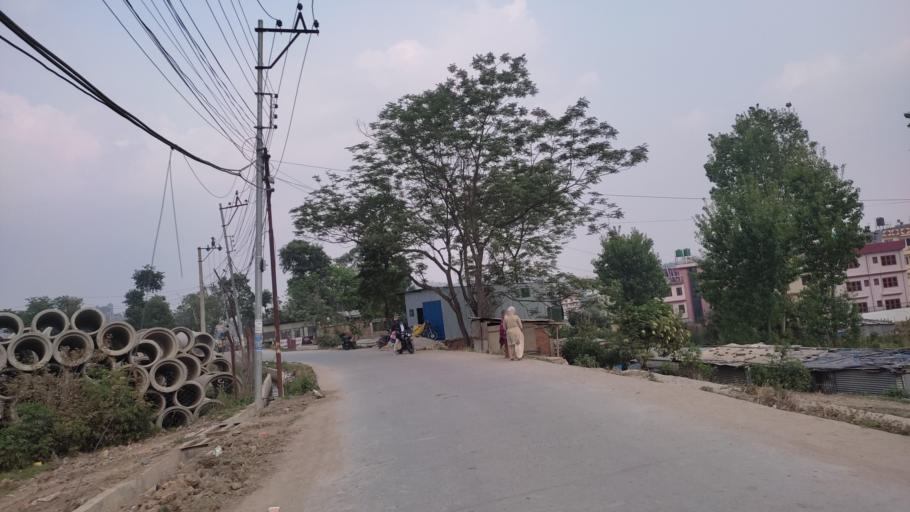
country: NP
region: Central Region
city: Kirtipur
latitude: 27.6806
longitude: 85.2539
